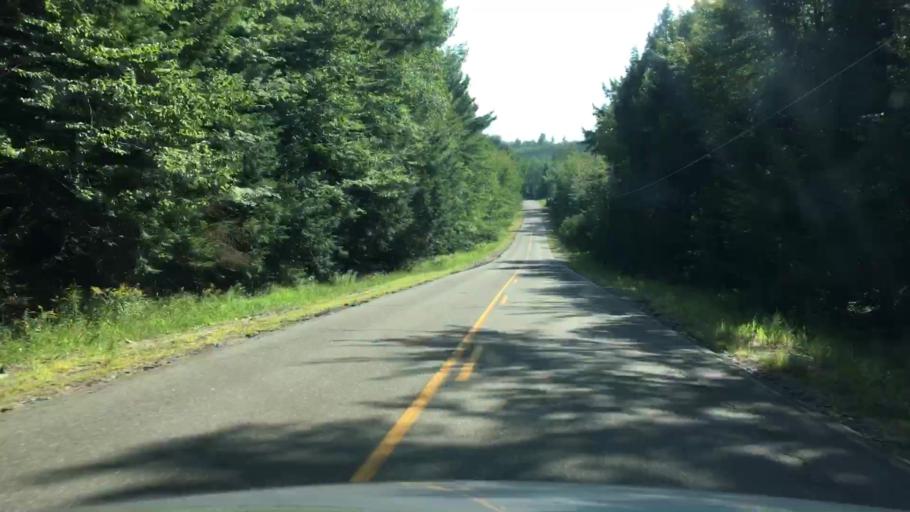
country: US
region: Maine
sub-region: Penobscot County
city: Enfield
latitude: 45.2963
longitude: -68.5542
